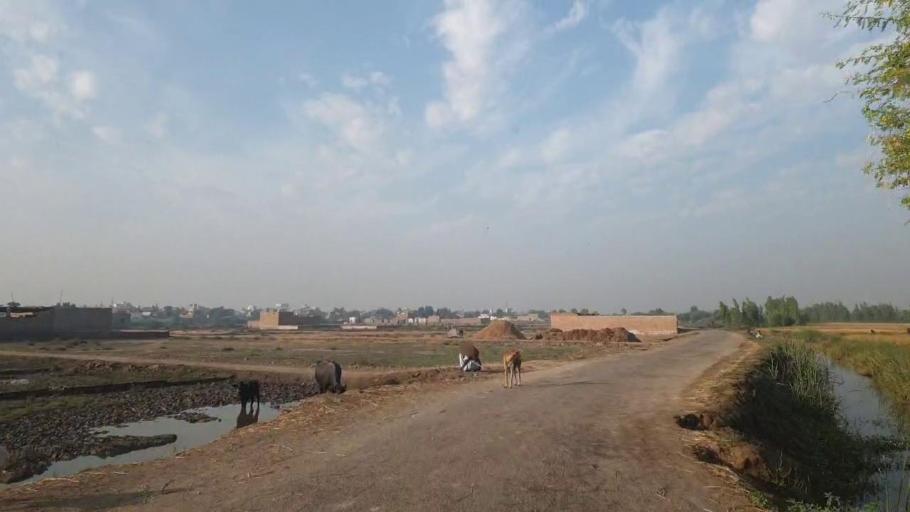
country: PK
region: Sindh
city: Tando Bago
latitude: 24.7953
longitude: 68.9690
